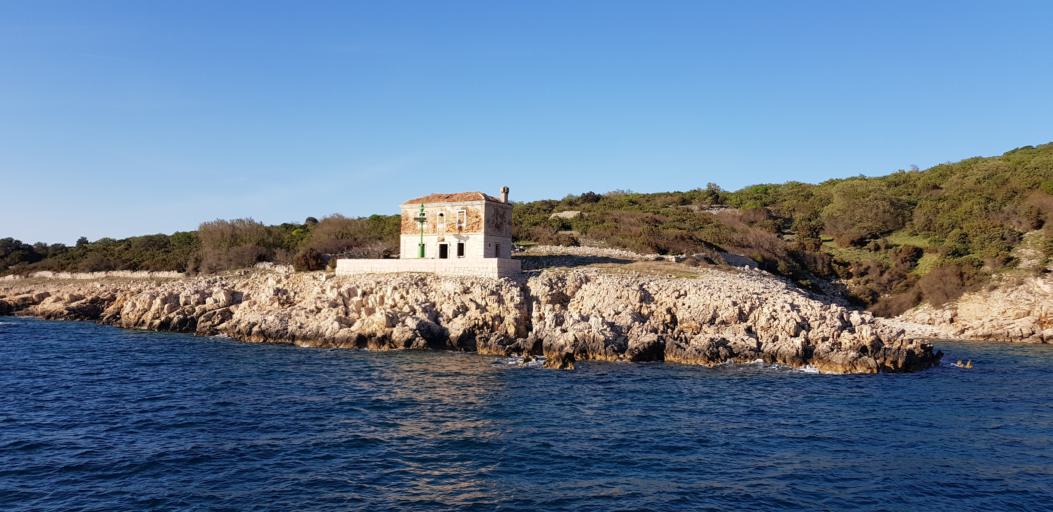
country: HR
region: Primorsko-Goranska
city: Punat
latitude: 44.9789
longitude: 14.6172
